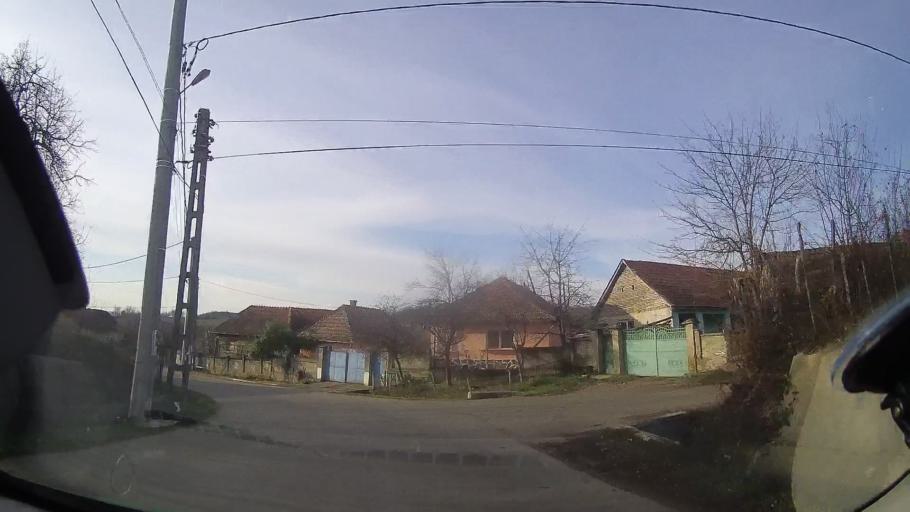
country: RO
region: Bihor
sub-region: Comuna Sarbi
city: Burzuc
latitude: 47.1103
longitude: 22.1734
